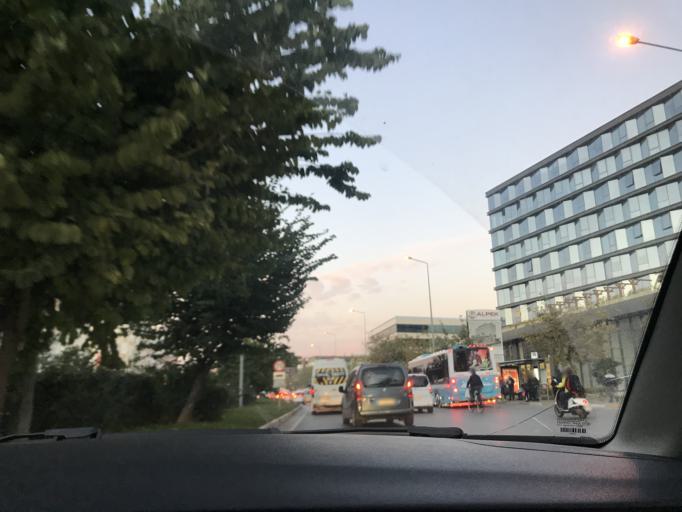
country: TR
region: Antalya
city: Antalya
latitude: 36.8999
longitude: 30.7158
